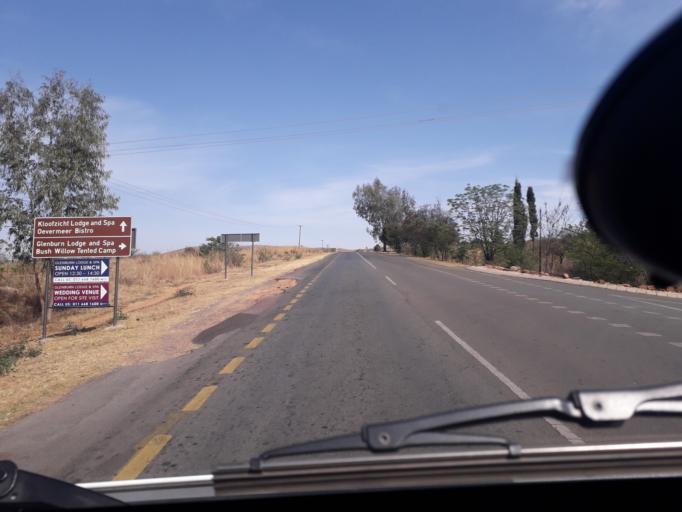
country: ZA
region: Gauteng
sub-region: West Rand District Municipality
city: Muldersdriseloop
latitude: -25.9888
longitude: 27.8376
